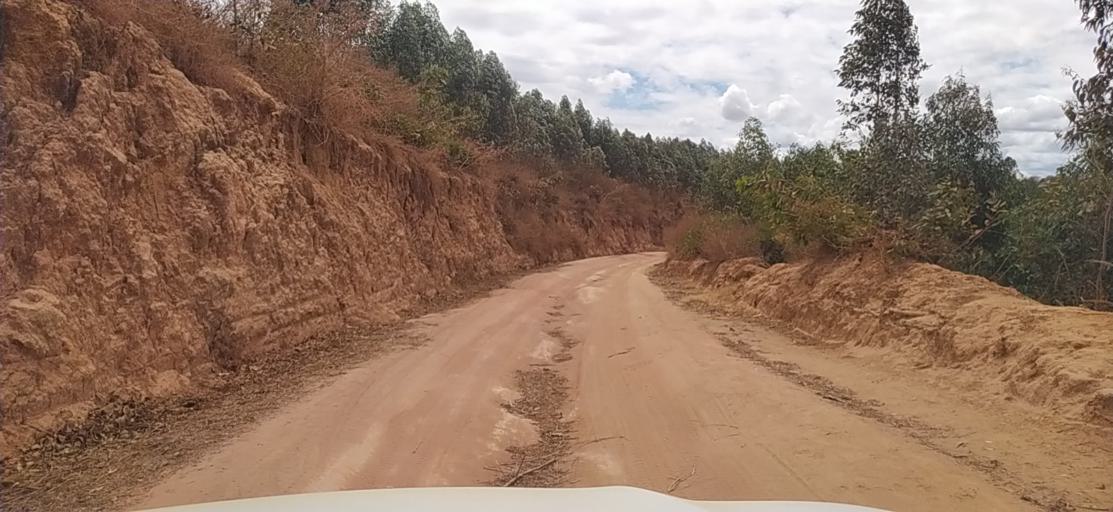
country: MG
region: Alaotra Mangoro
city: Ambatondrazaka
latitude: -18.0083
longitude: 48.2596
